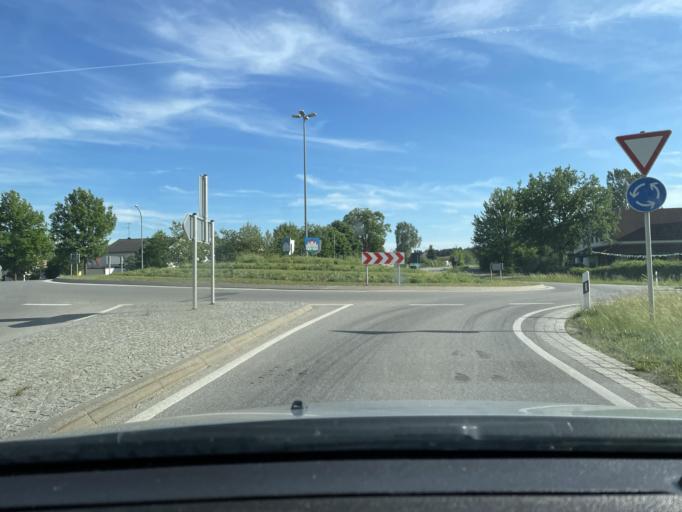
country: DE
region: Bavaria
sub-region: Lower Bavaria
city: Siegenburg
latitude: 48.7618
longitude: 11.8369
